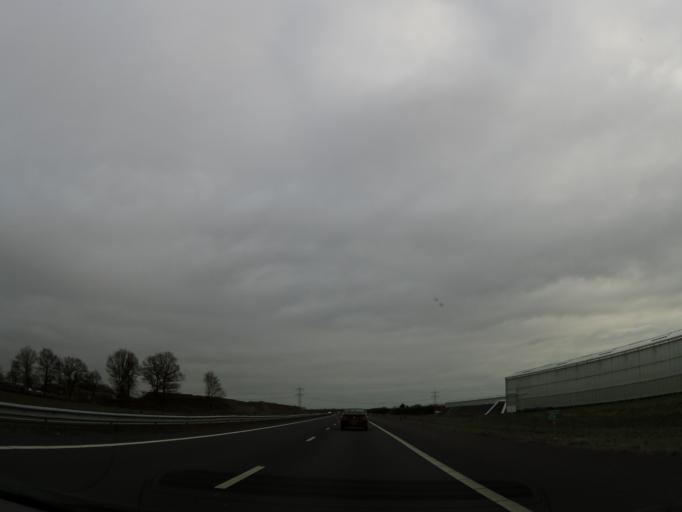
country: NL
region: Limburg
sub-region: Gemeente Peel en Maas
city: Maasbree
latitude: 51.4391
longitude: 6.0870
